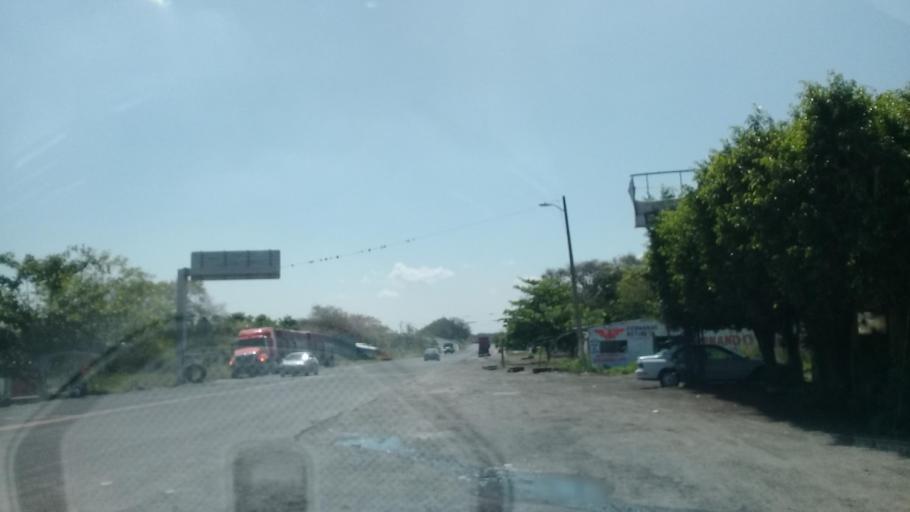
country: MX
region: Veracruz
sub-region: Emiliano Zapata
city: Plan del Rio
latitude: 19.3932
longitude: -96.6186
